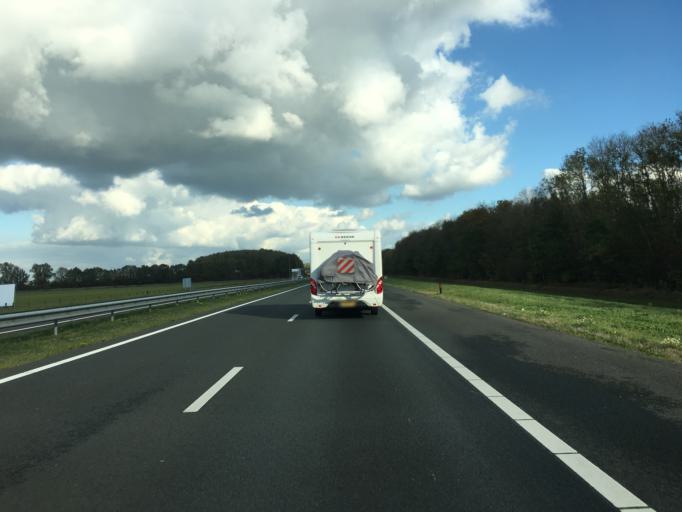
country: NL
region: Gelderland
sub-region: Gemeente Zevenaar
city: Zevenaar
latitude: 51.9213
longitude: 6.1484
